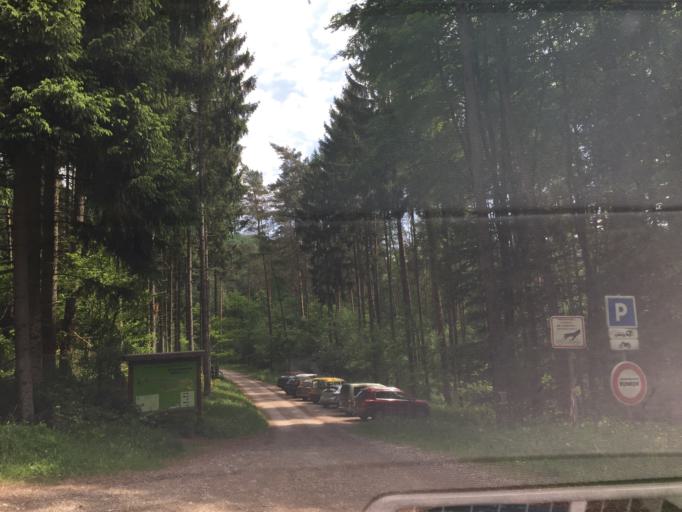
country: DE
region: Rheinland-Pfalz
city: Nothweiler
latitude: 49.0474
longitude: 7.7788
